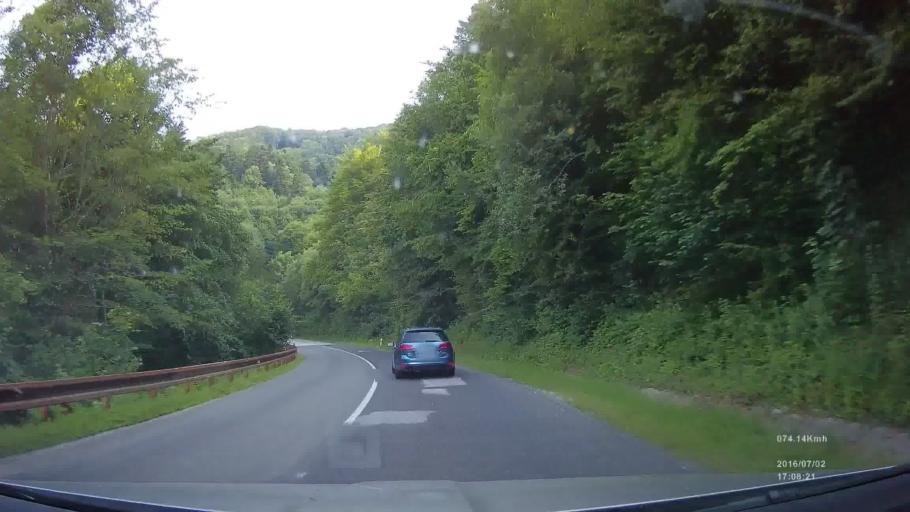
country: SK
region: Kosicky
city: Gelnica
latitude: 48.8384
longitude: 21.0367
